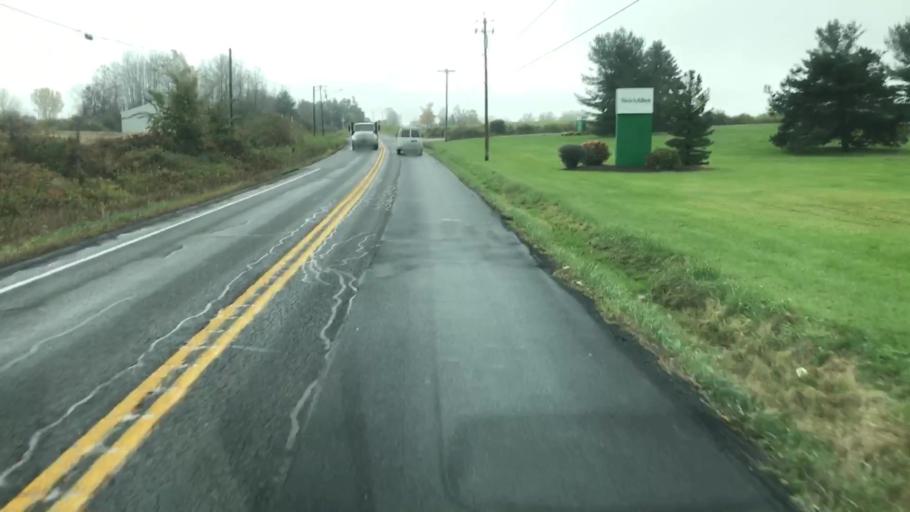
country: US
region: New York
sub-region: Onondaga County
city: Skaneateles
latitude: 42.9773
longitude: -76.4279
